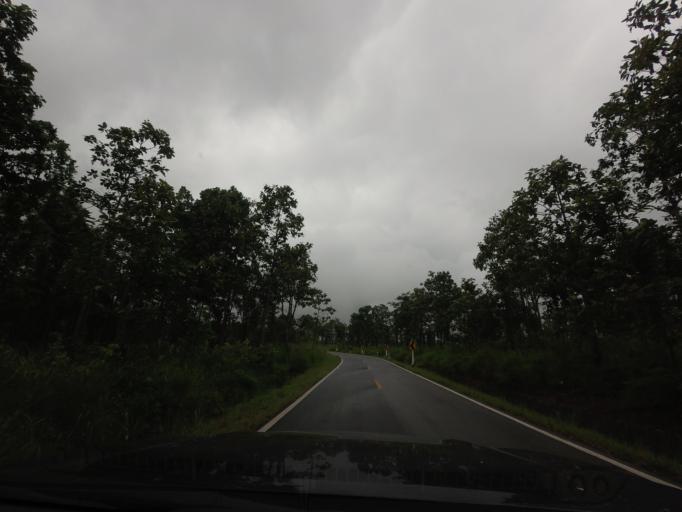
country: TH
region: Nong Khai
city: Sangkhom
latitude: 18.0347
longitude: 102.3382
